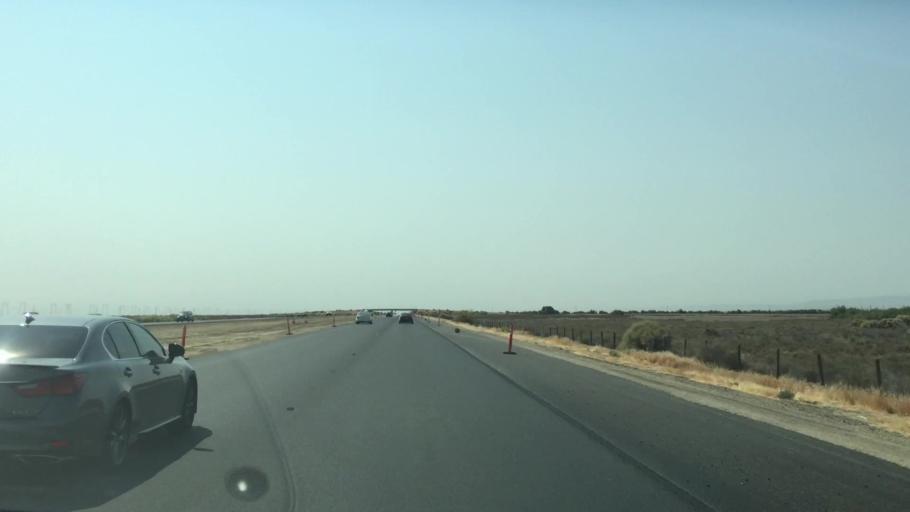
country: US
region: California
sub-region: Kern County
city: Lost Hills
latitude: 35.8000
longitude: -119.7903
